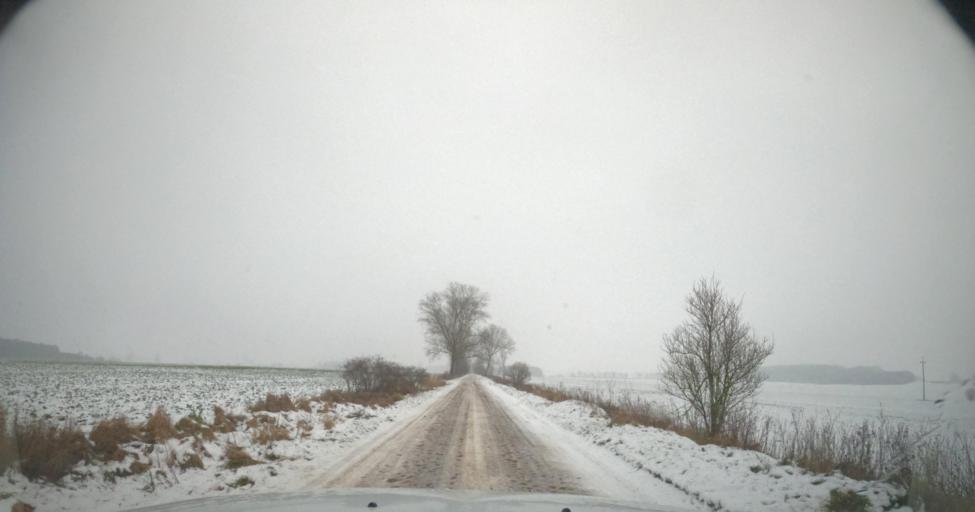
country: PL
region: West Pomeranian Voivodeship
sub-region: Powiat gryficki
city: Brojce
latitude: 53.9008
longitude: 15.3211
